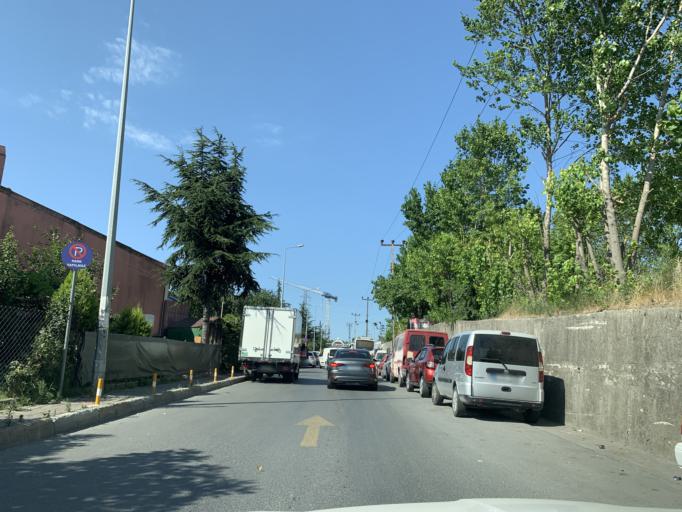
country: TR
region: Istanbul
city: Esenyurt
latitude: 41.0627
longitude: 28.6639
